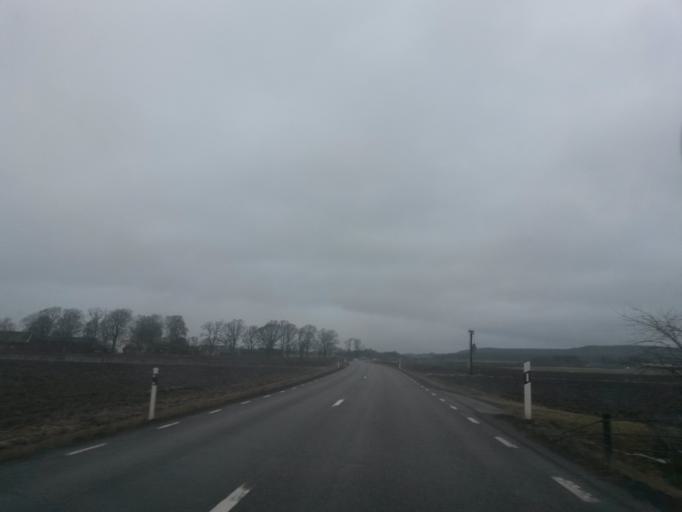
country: SE
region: Vaestra Goetaland
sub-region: Vanersborgs Kommun
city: Vargon
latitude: 58.2774
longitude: 12.3986
